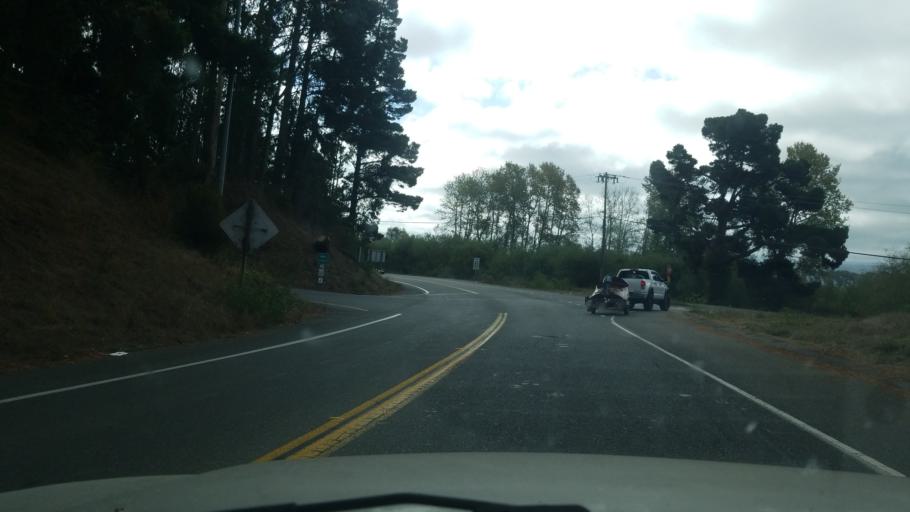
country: US
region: California
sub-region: Humboldt County
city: Fortuna
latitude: 40.6206
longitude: -124.2101
